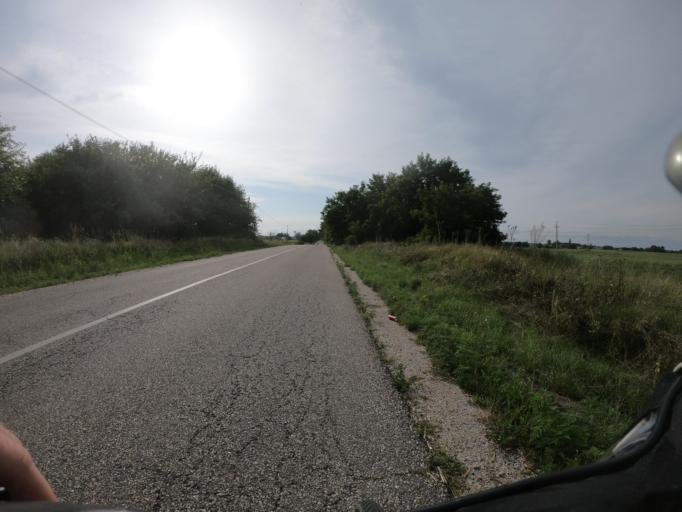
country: HU
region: Borsod-Abauj-Zemplen
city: Mezocsat
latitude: 47.8166
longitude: 20.9283
